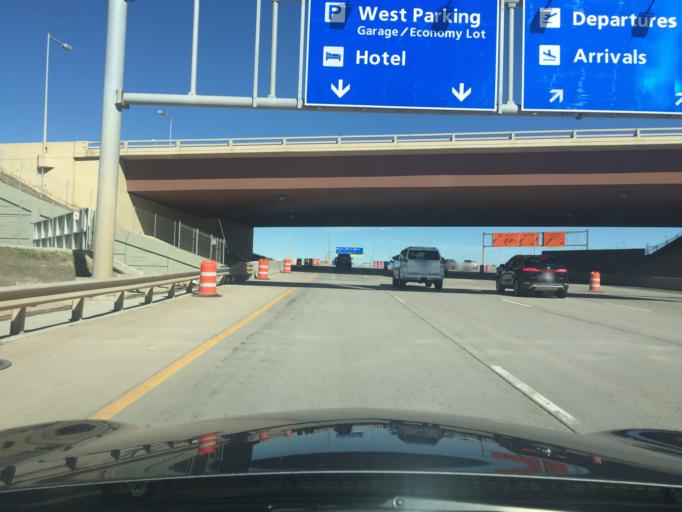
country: US
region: Colorado
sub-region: Weld County
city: Lochbuie
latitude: 39.8420
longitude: -104.6734
